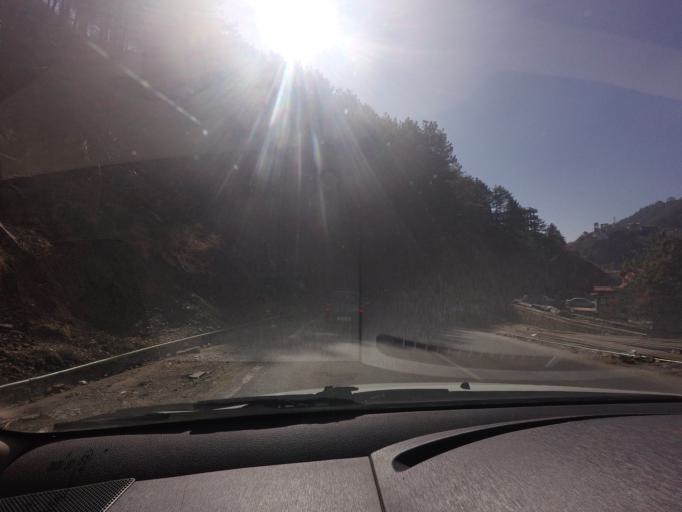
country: IN
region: Himachal Pradesh
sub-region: Shimla
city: Shimla
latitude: 31.1081
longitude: 77.1985
